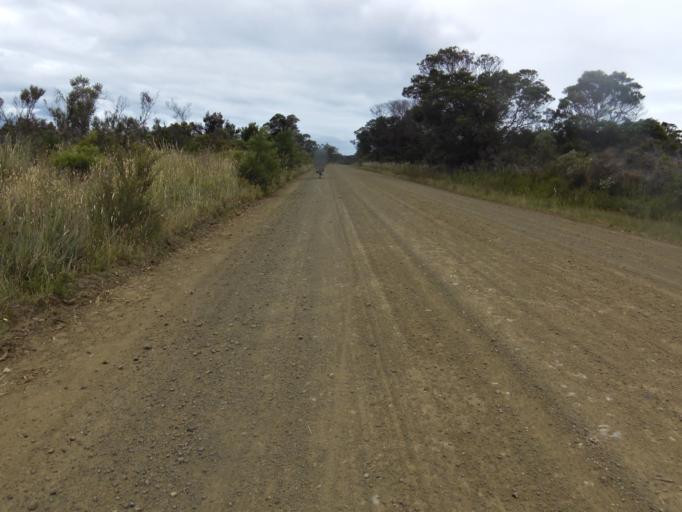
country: AU
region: Victoria
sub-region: Bass Coast
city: Cowes
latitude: -38.3826
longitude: 145.2887
